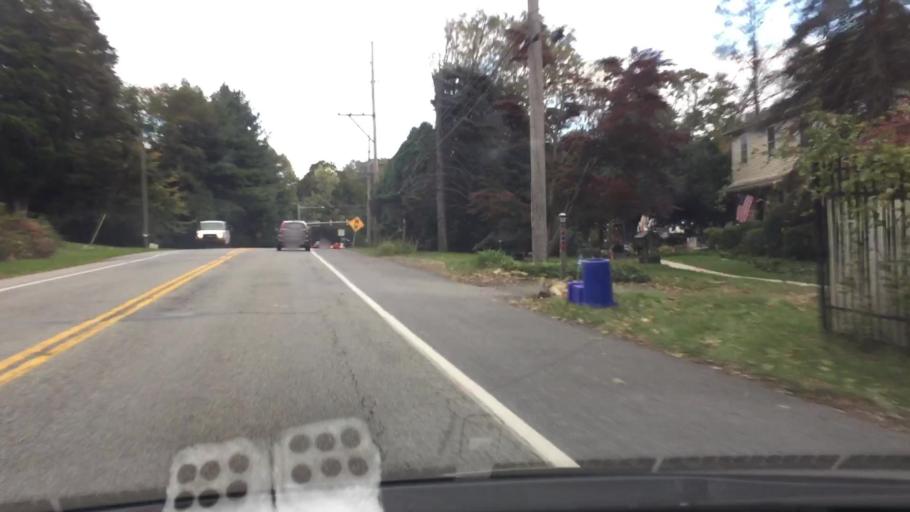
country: US
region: Pennsylvania
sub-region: Delaware County
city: Lima
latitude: 39.9335
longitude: -75.4505
